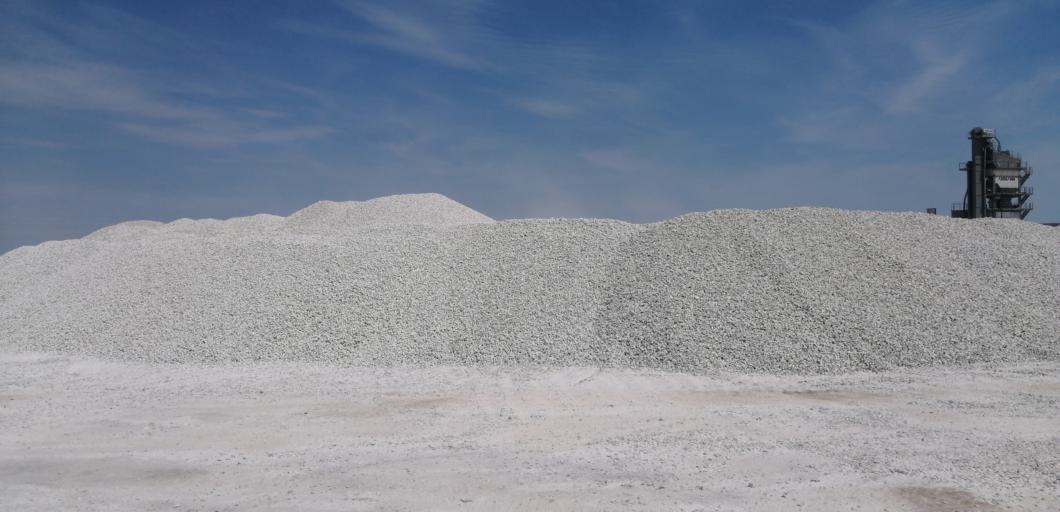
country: KZ
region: Qaraghandy
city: Balqash
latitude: 46.6284
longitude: 74.3747
